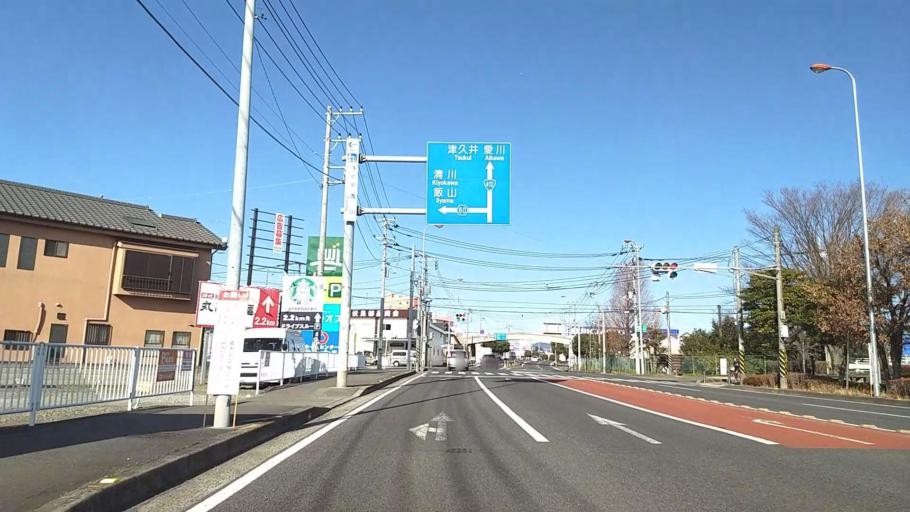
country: JP
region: Kanagawa
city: Atsugi
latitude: 35.4520
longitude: 139.3540
